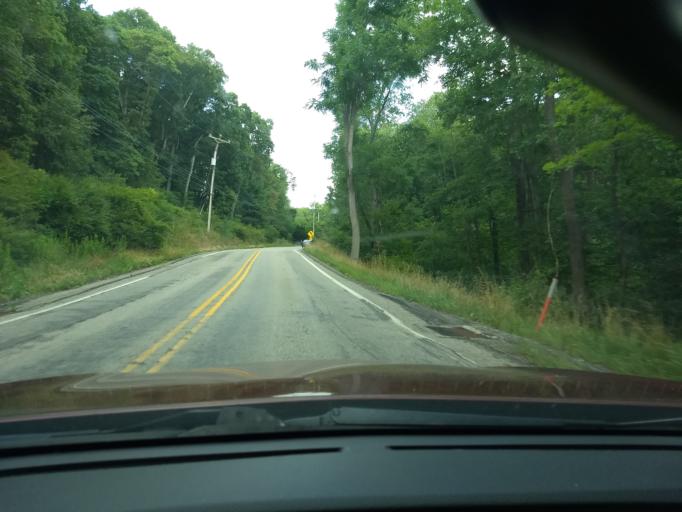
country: US
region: Pennsylvania
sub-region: Allegheny County
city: Curtisville
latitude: 40.6564
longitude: -79.8868
